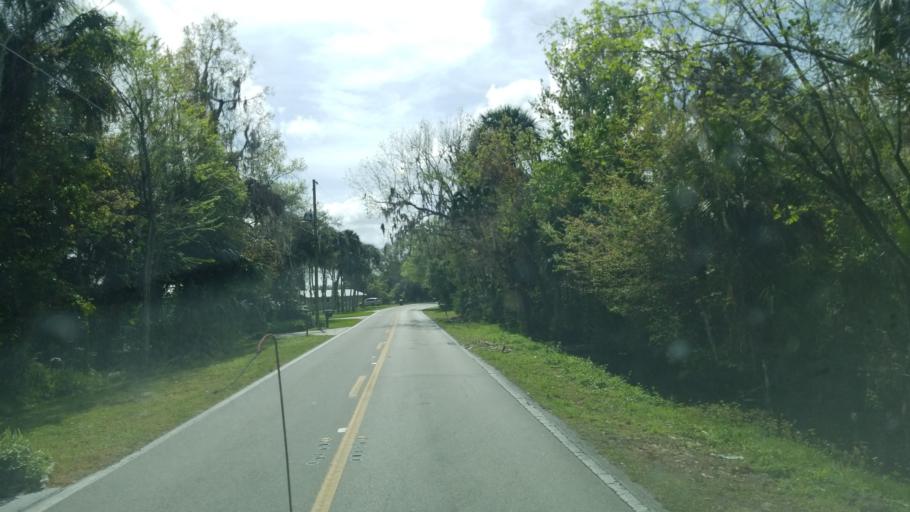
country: US
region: Florida
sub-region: Polk County
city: Dundee
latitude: 27.9907
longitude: -81.5499
